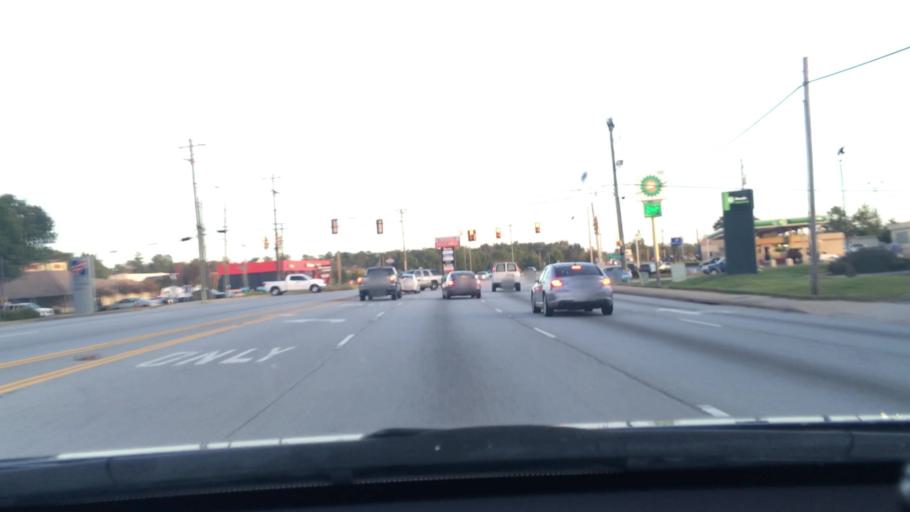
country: US
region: South Carolina
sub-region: Richland County
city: Forest Acres
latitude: 33.9696
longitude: -80.9473
